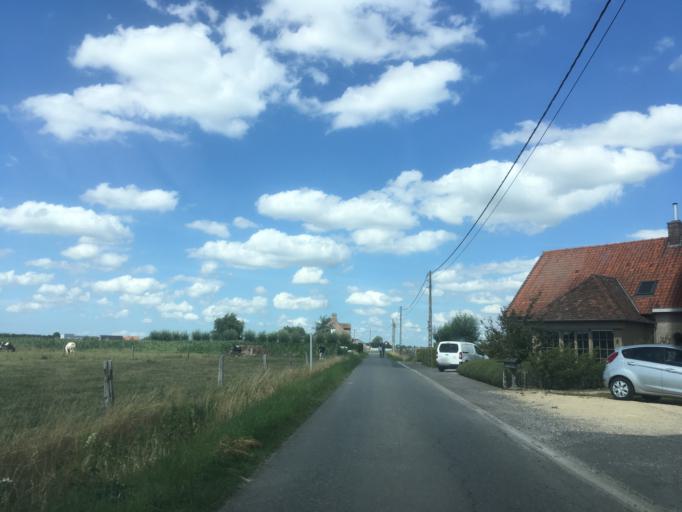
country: BE
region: Flanders
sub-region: Provincie West-Vlaanderen
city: Staden
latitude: 50.9335
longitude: 3.0380
